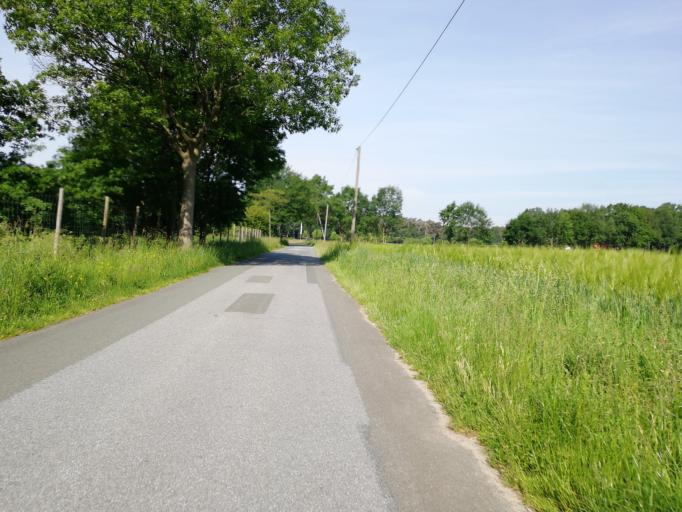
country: DE
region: North Rhine-Westphalia
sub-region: Regierungsbezirk Detmold
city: Verl
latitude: 51.9035
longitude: 8.5081
